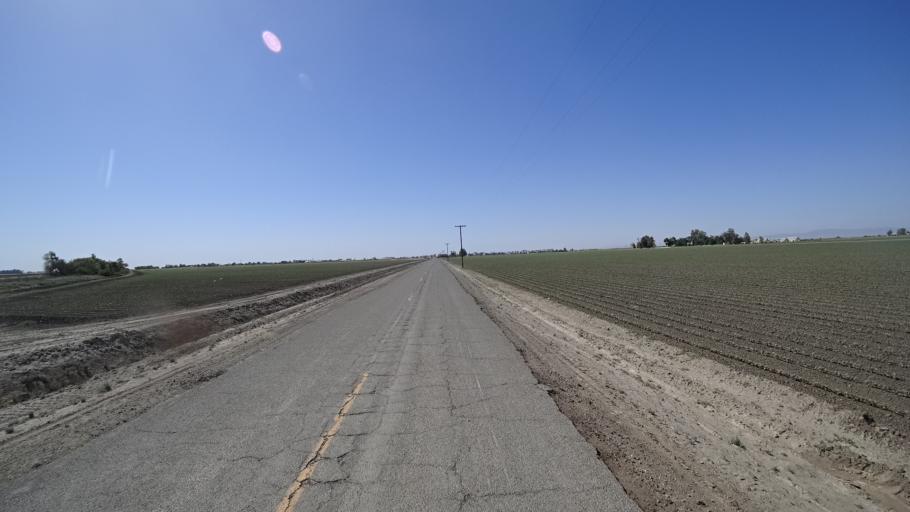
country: US
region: California
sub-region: Kings County
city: Stratford
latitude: 36.2106
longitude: -119.8340
